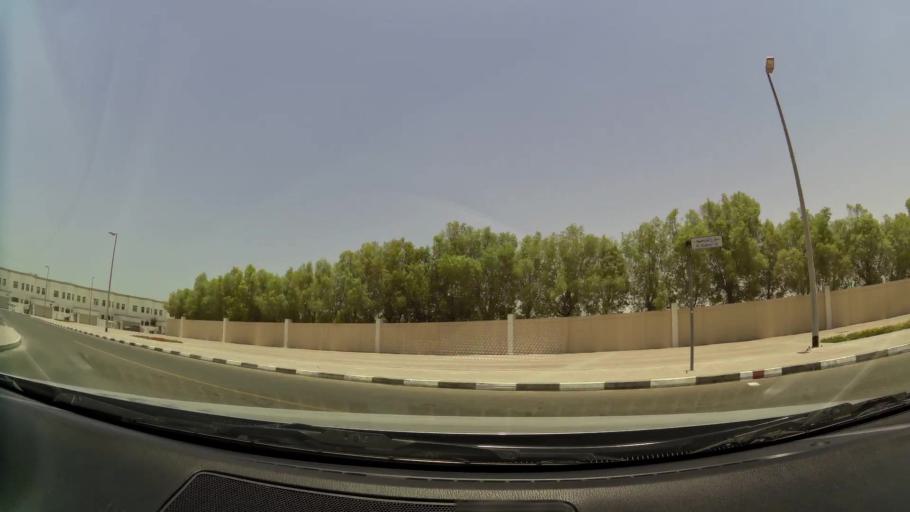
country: AE
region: Dubai
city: Dubai
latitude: 25.1750
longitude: 55.2251
